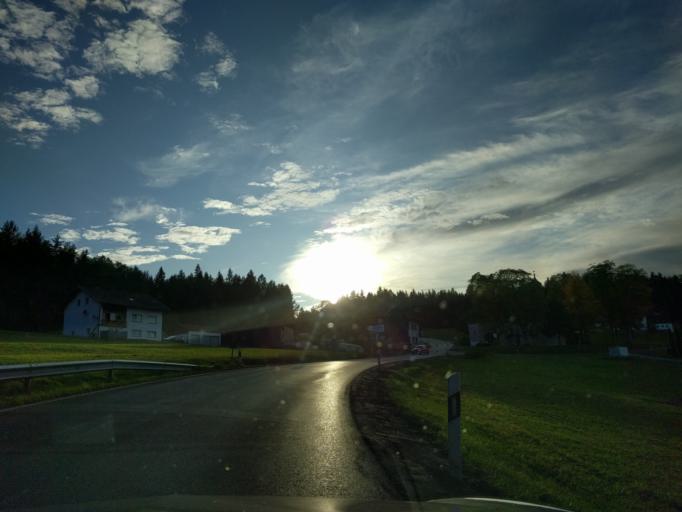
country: DE
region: Bavaria
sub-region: Upper Palatinate
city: Grafenwiesen
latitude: 49.1957
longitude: 12.9056
